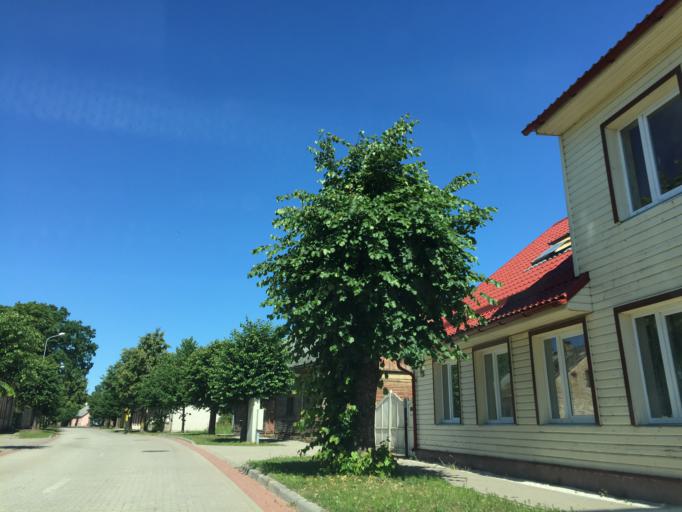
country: LV
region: Ventspils Rajons
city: Piltene
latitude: 57.2269
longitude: 21.6752
